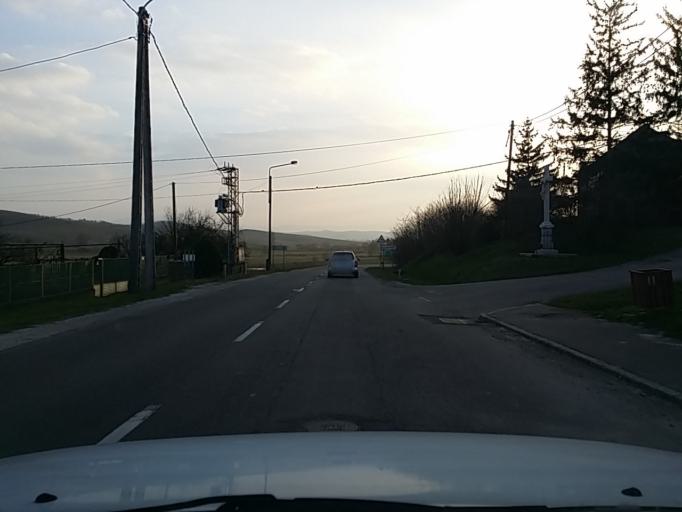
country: HU
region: Heves
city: Tarnalelesz
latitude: 48.0482
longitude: 20.1505
